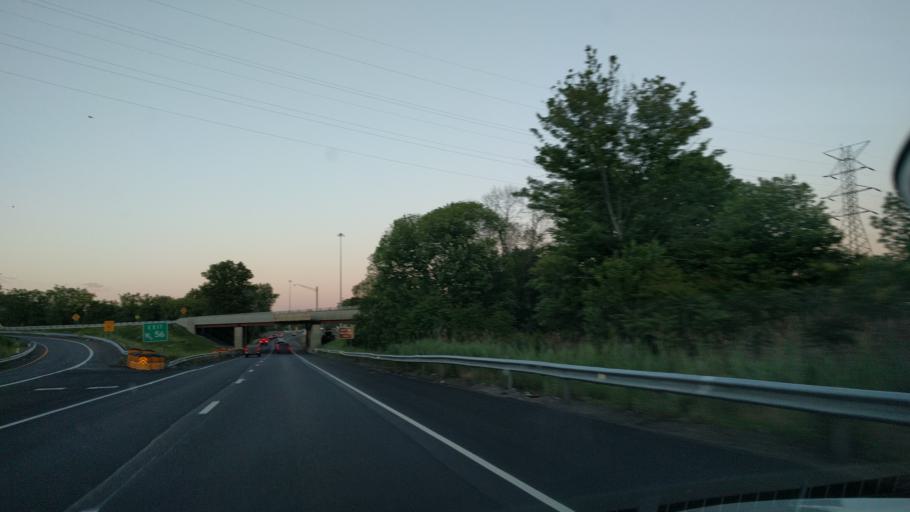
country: US
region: Connecticut
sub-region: Hartford County
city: Hartford
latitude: 41.7653
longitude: -72.6542
